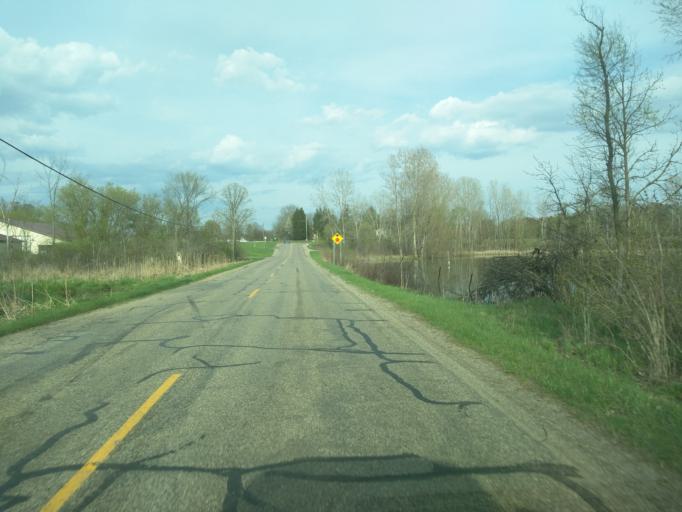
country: US
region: Michigan
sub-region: Eaton County
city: Dimondale
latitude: 42.6257
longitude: -84.6259
